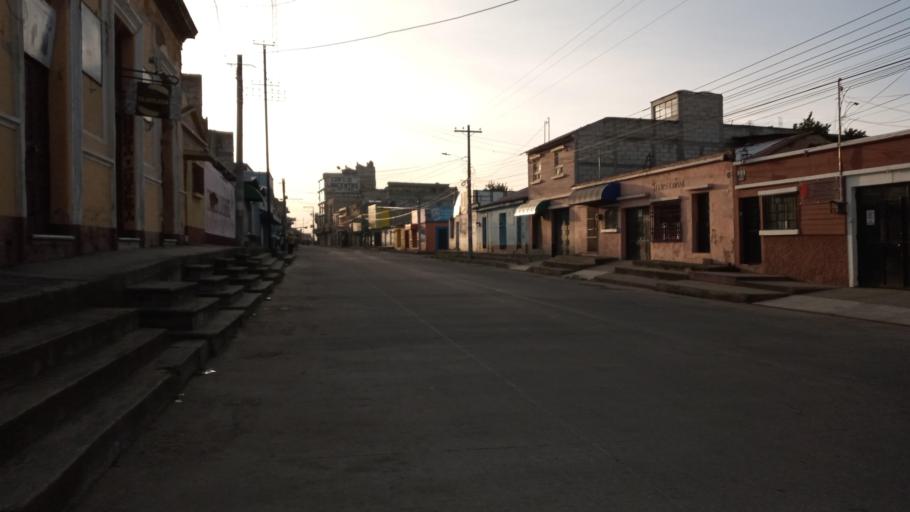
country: GT
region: Quetzaltenango
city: Quetzaltenango
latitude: 14.8403
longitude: -91.5225
